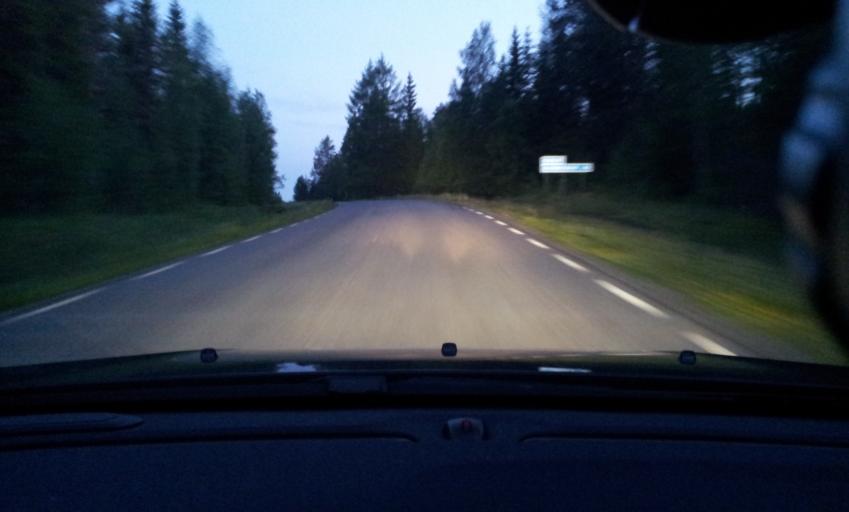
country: SE
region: Jaemtland
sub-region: Braecke Kommun
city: Braecke
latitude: 62.7336
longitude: 15.1670
